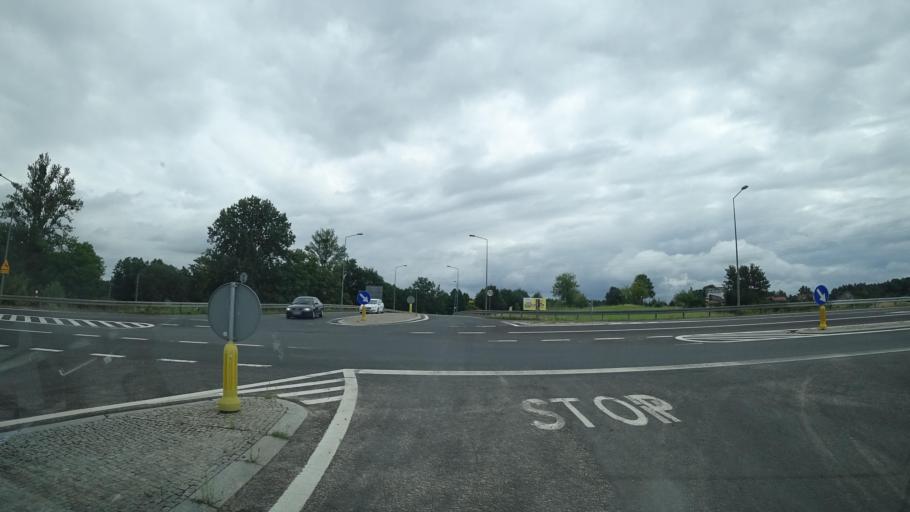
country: PL
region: Warmian-Masurian Voivodeship
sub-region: Powiat olecki
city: Olecko
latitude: 54.0638
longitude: 22.4815
